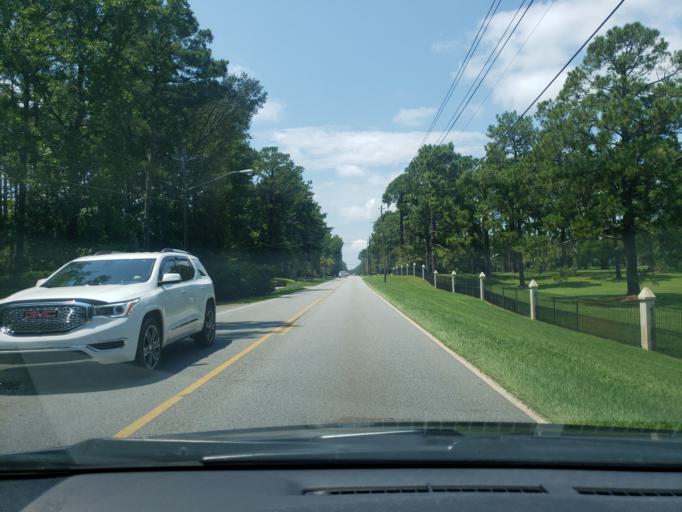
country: US
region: Georgia
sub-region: Dougherty County
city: Albany
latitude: 31.6135
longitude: -84.2376
